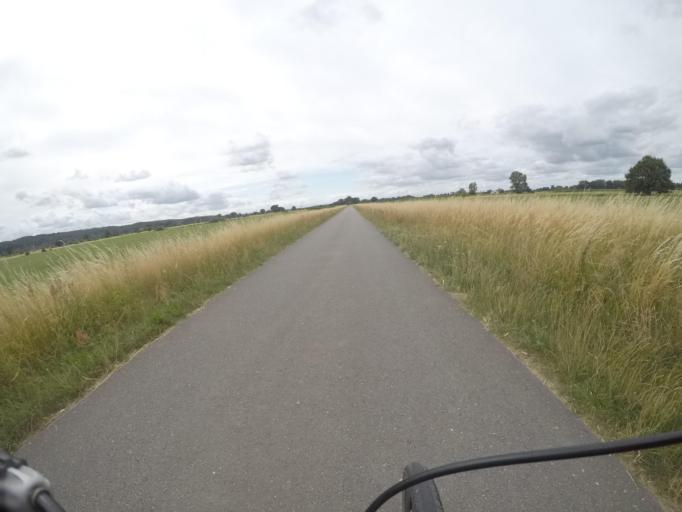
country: DE
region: Lower Saxony
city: Neu Darchau
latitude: 53.2225
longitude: 10.9528
